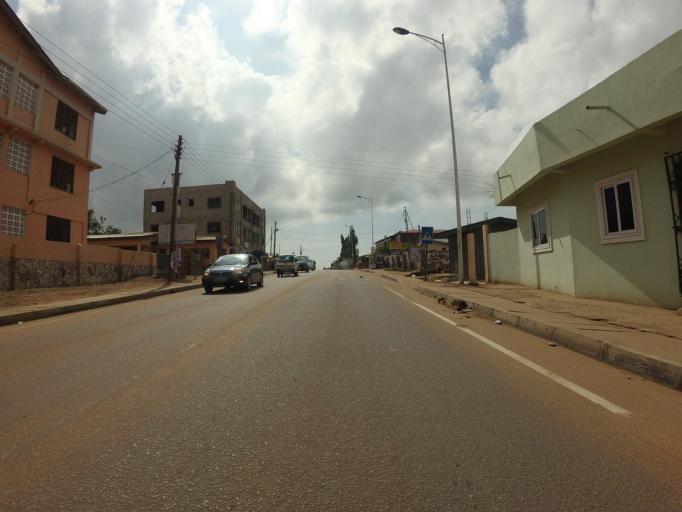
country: GH
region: Greater Accra
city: Teshi Old Town
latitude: 5.5947
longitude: -0.1287
